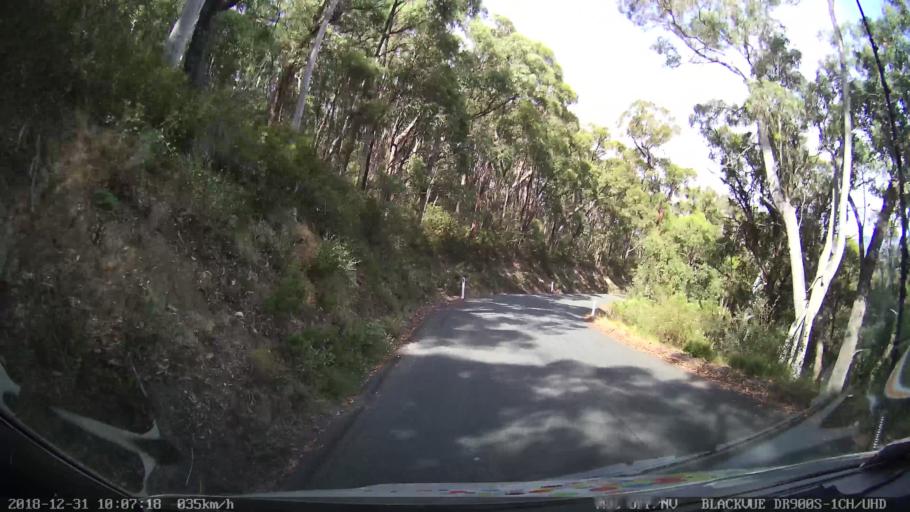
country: AU
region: New South Wales
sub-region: Snowy River
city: Jindabyne
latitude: -36.5314
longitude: 148.1846
